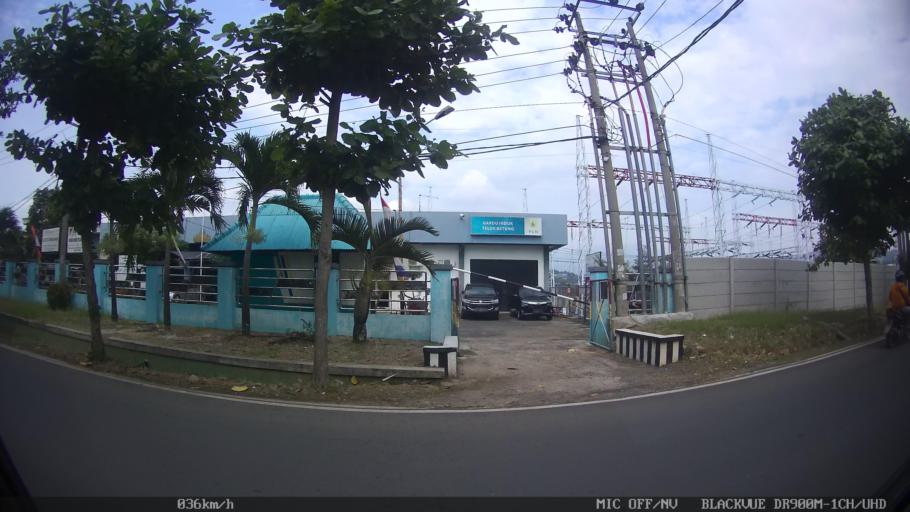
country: ID
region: Lampung
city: Bandarlampung
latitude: -5.4396
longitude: 105.2541
